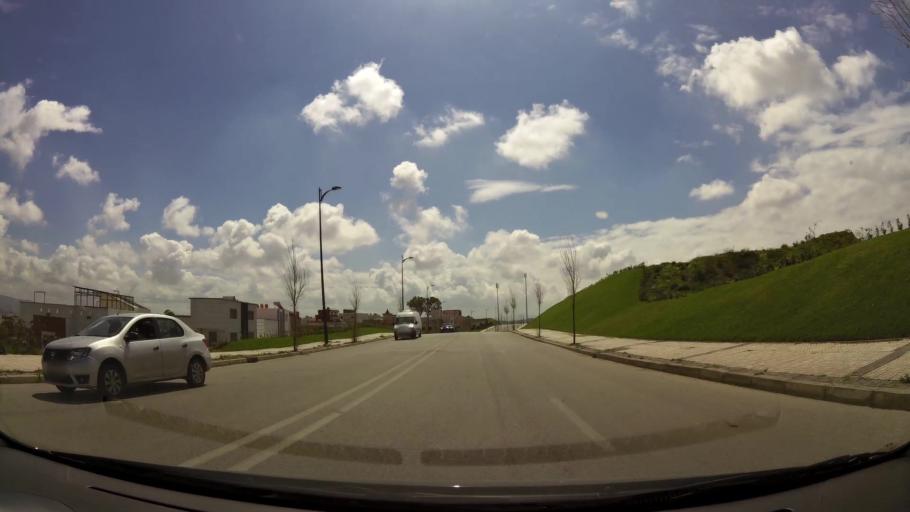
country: MA
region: Tanger-Tetouan
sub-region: Tanger-Assilah
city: Tangier
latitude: 35.7708
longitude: -5.8401
